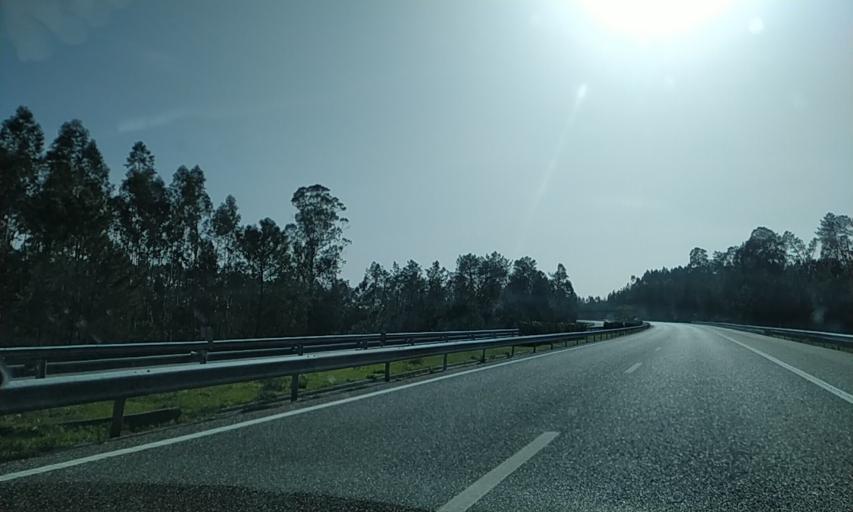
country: PT
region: Coimbra
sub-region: Soure
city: Soure
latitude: 40.0077
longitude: -8.6041
